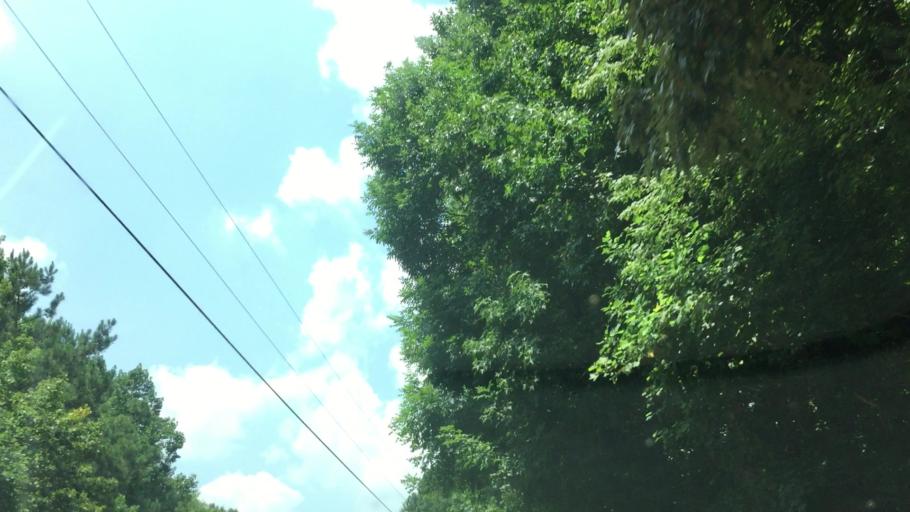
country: US
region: Georgia
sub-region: Carroll County
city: Villa Rica
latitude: 33.6172
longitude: -84.9488
